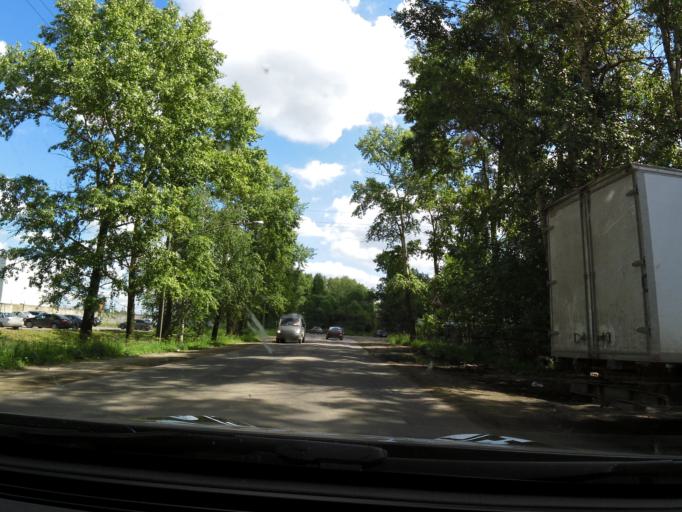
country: RU
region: Vologda
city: Vologda
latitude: 59.2377
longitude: 39.8156
